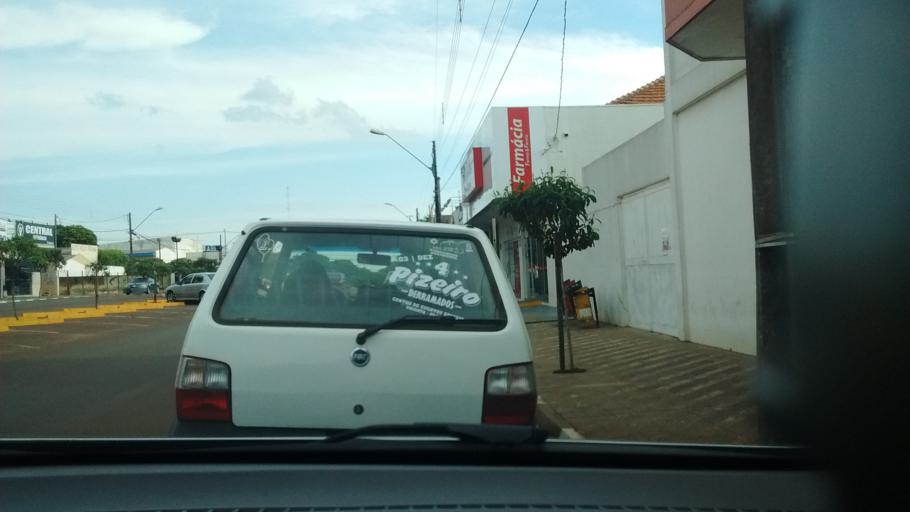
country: BR
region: Parana
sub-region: Corbelia
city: Corbelia
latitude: -24.5444
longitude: -52.9899
